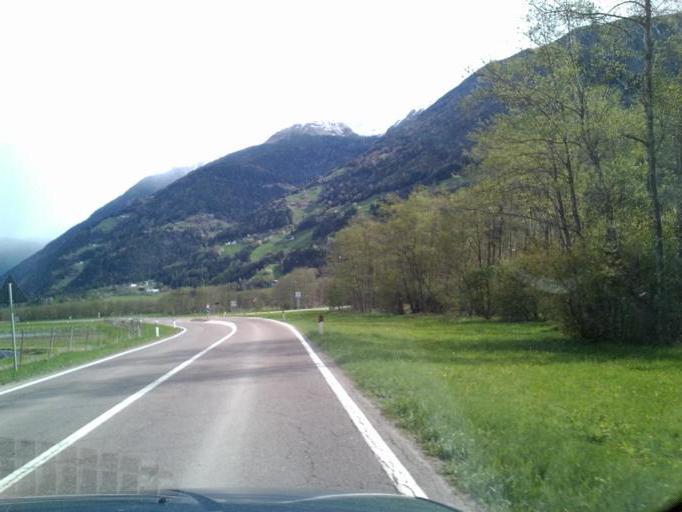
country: IT
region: Trentino-Alto Adige
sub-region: Bolzano
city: Gais
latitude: 46.8462
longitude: 11.9487
